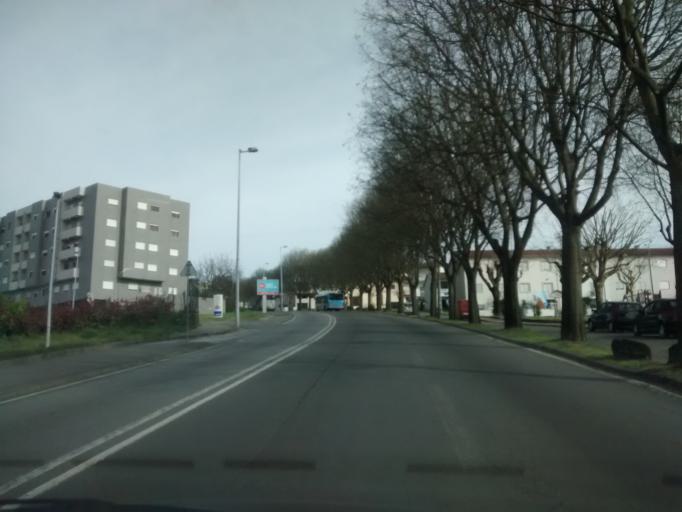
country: PT
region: Braga
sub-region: Braga
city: Braga
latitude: 41.5570
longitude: -8.4409
